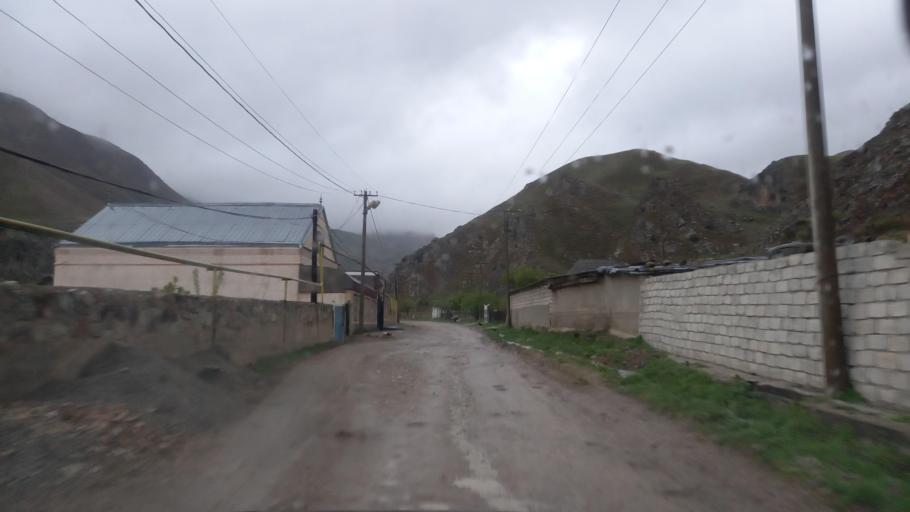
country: RU
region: Kabardino-Balkariya
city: Bylym
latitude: 43.4526
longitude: 43.0283
